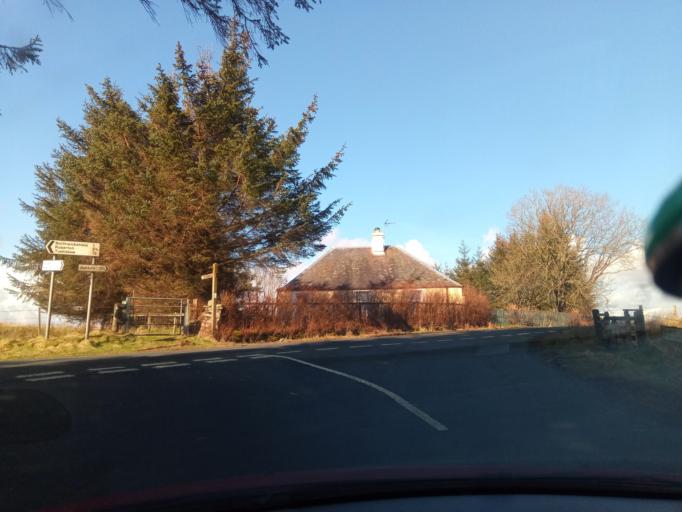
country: GB
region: Scotland
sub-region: The Scottish Borders
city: Hawick
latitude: 55.4407
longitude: -2.8846
